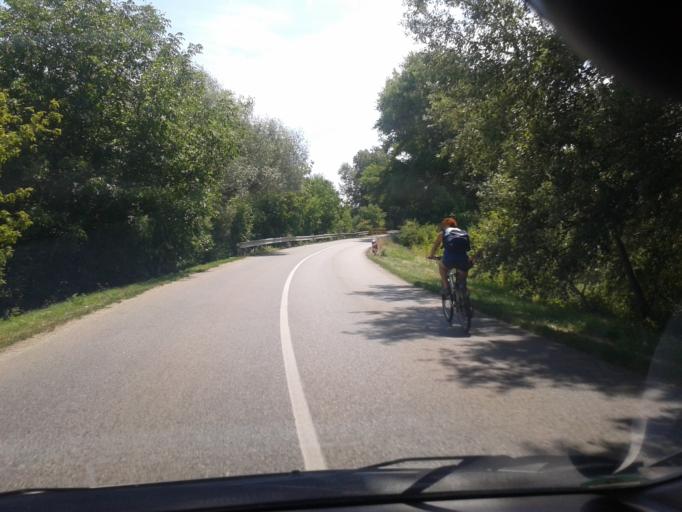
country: SK
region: Nitriansky
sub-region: Okres Nove Zamky
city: Sturovo
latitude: 47.8137
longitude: 18.7218
